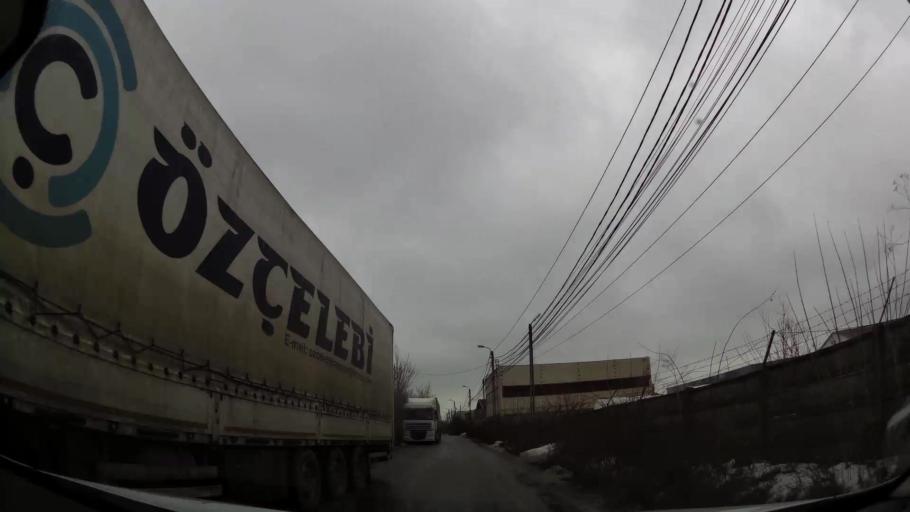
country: RO
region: Ilfov
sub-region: Comuna Chitila
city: Chitila
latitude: 44.4952
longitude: 26.0060
